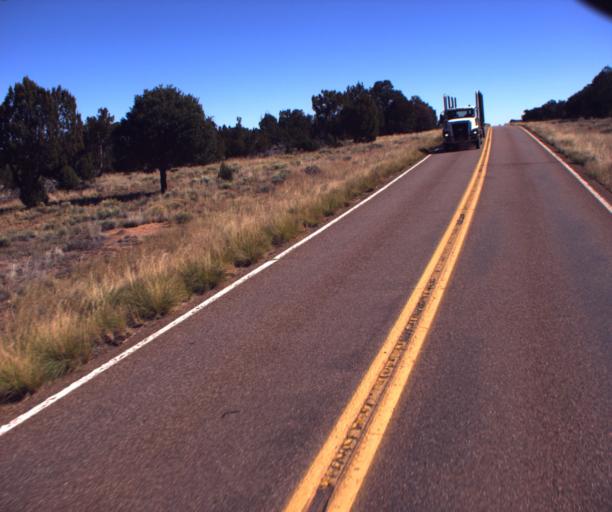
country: US
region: Arizona
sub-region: Navajo County
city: Heber-Overgaard
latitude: 34.4530
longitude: -110.4552
